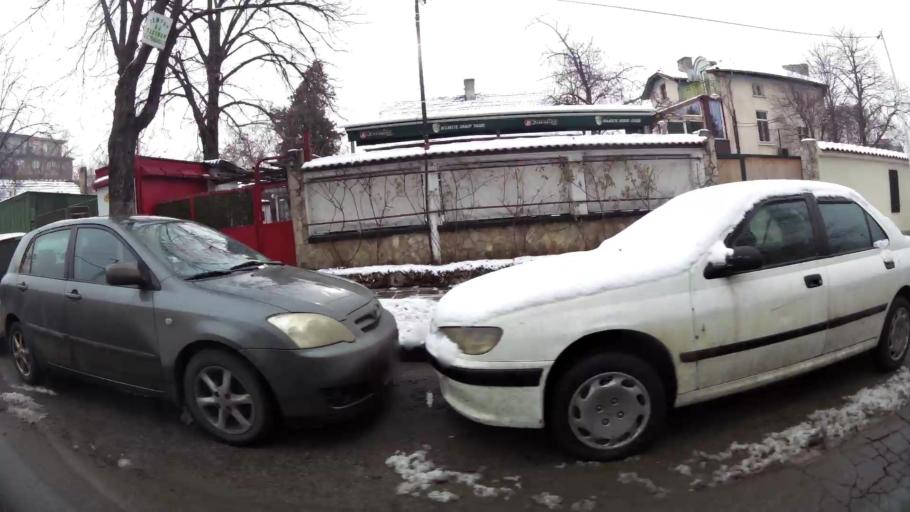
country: BG
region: Sofia-Capital
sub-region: Stolichna Obshtina
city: Sofia
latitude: 42.7081
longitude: 23.3038
